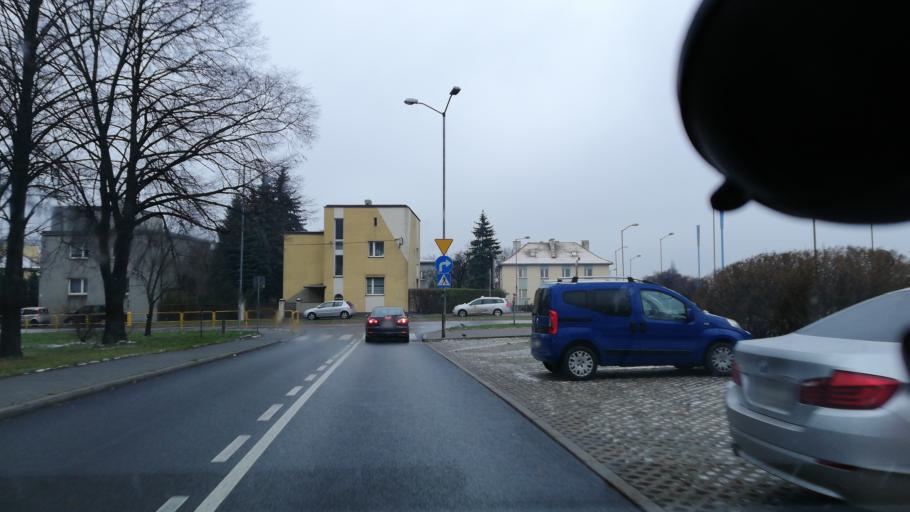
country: PL
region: Silesian Voivodeship
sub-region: Swietochlowice
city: Swietochlowice
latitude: 50.2856
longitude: 18.9414
